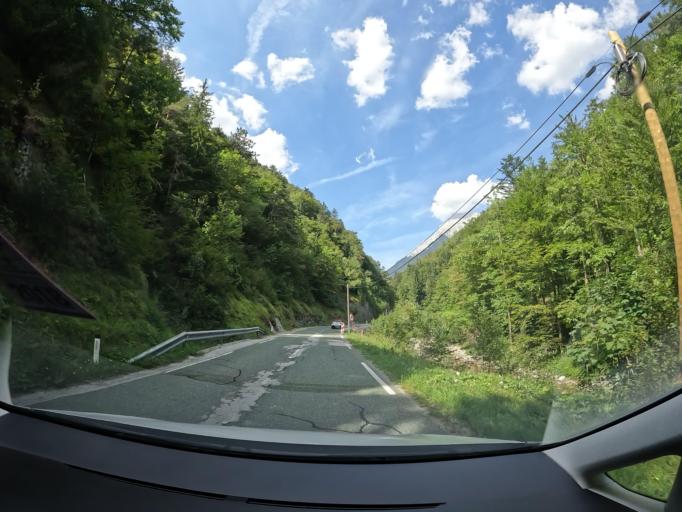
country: SI
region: Cerklje na Gorenjskem
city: Cerklje na Gorenjskem
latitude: 46.3105
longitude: 14.5003
